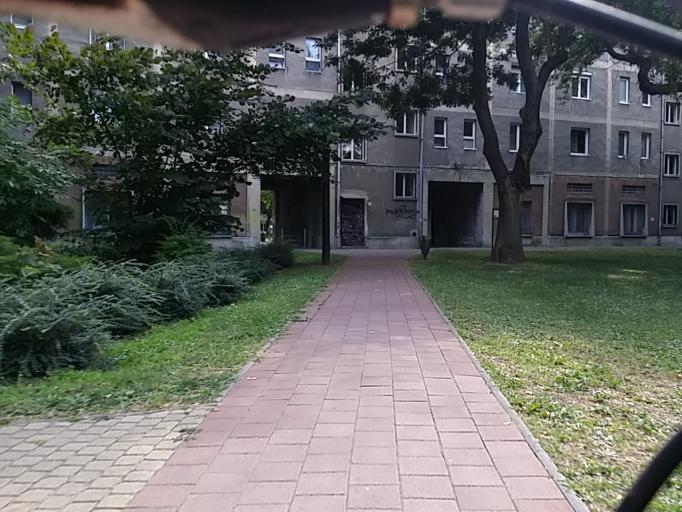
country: HU
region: Budapest
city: Budapest XIII. keruelet
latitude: 47.5400
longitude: 19.0844
